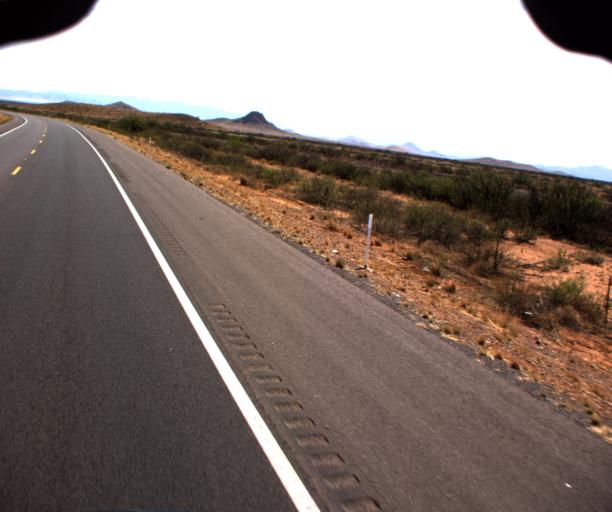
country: US
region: Arizona
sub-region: Cochise County
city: Tombstone
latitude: 31.9037
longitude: -109.7955
